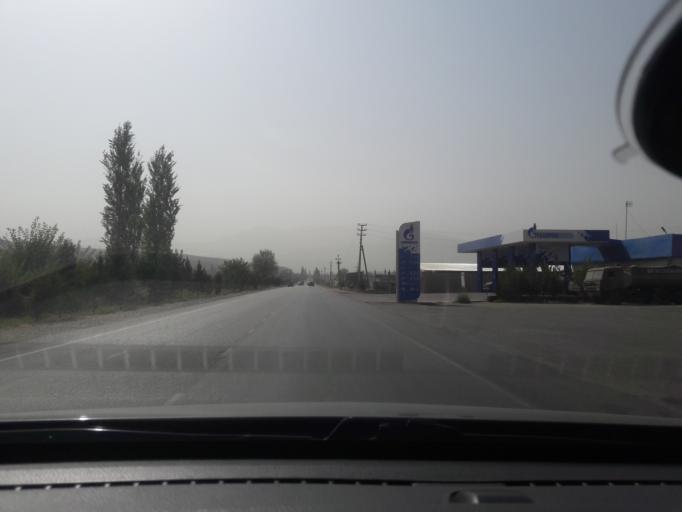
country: TJ
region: Republican Subordination
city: Vahdat
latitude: 38.5315
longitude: 69.0256
